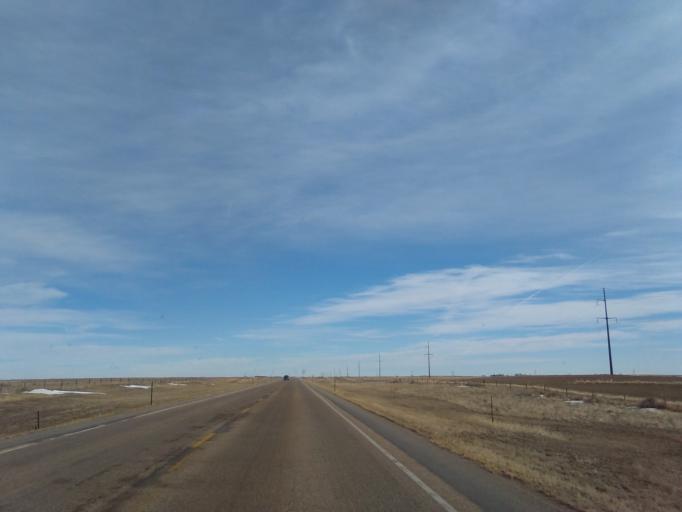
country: US
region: Wyoming
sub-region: Laramie County
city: Pine Bluffs
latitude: 41.4246
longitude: -104.3930
